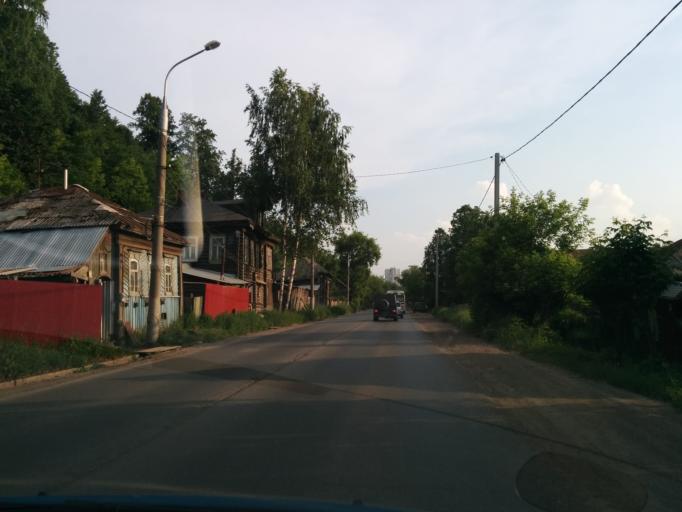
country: RU
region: Perm
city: Perm
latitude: 58.0432
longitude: 56.3196
